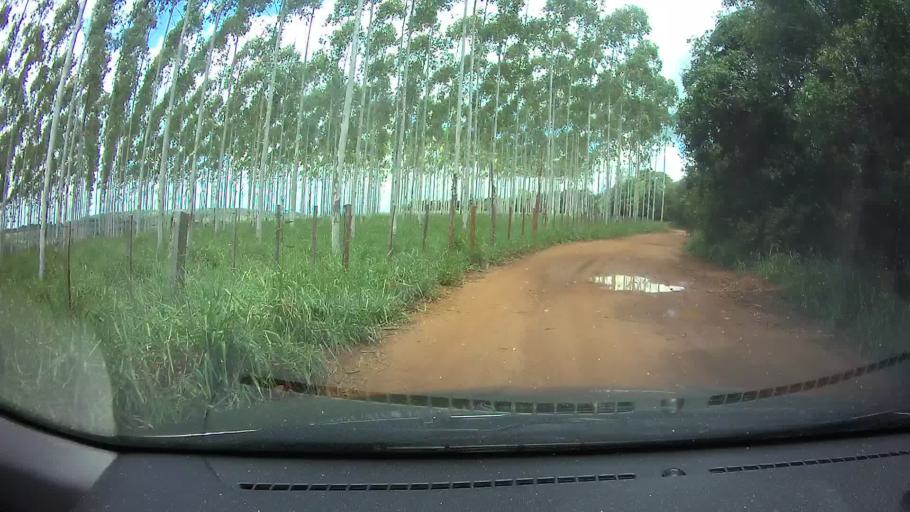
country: PY
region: Paraguari
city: La Colmena
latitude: -25.9659
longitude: -56.7350
